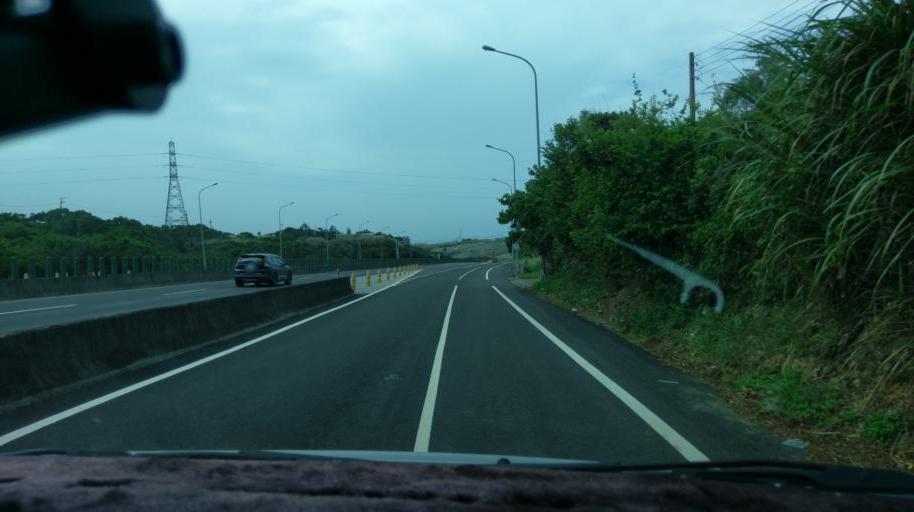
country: TW
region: Taiwan
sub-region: Miaoli
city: Miaoli
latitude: 24.5860
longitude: 120.7289
